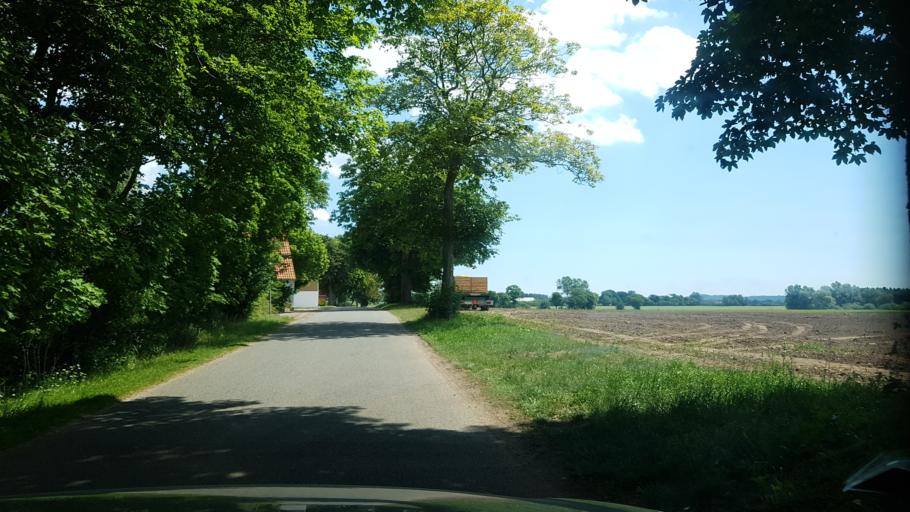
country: DK
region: Zealand
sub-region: Kalundborg Kommune
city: Svebolle
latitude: 55.7062
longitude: 11.2805
